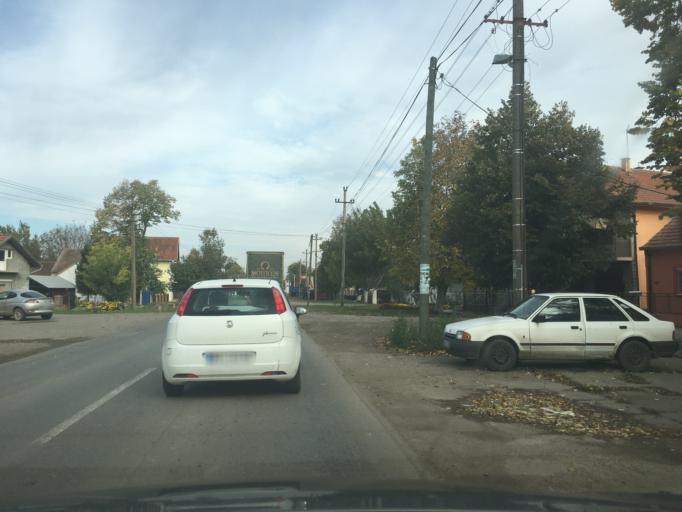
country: RS
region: Autonomna Pokrajina Vojvodina
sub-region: Juznobacki Okrug
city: Zabalj
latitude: 45.3595
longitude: 20.0655
